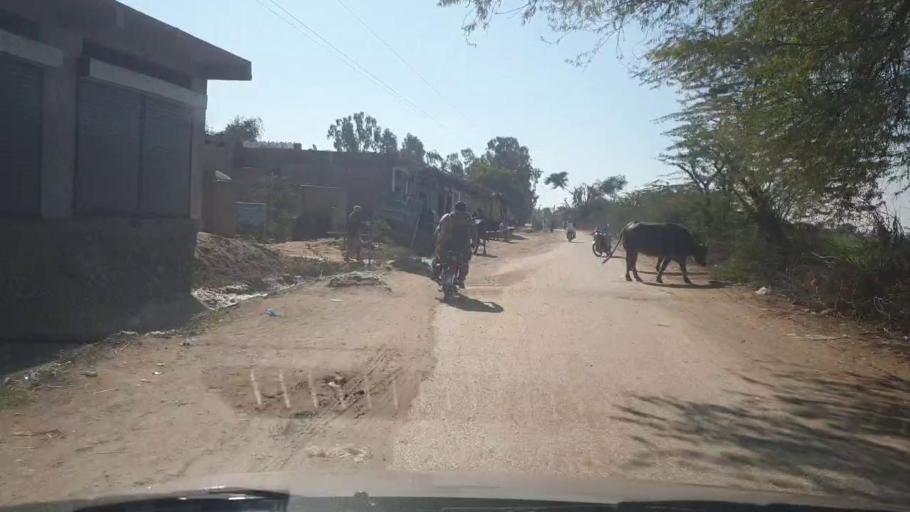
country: PK
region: Sindh
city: Bozdar
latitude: 27.0944
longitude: 68.6252
